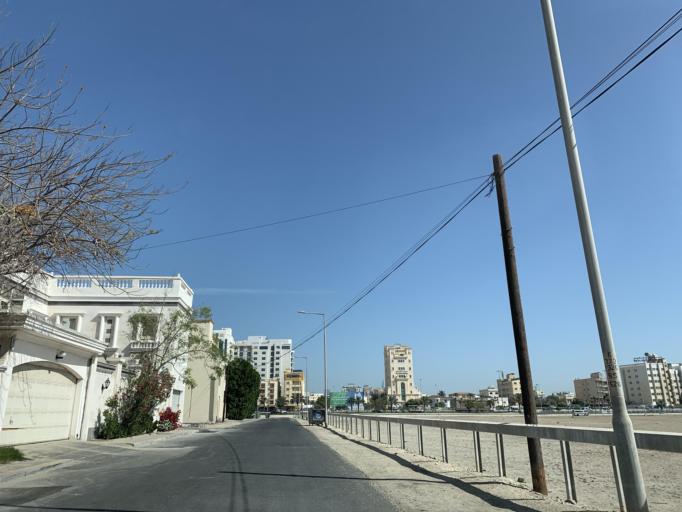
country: BH
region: Manama
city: Manama
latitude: 26.2019
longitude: 50.5765
